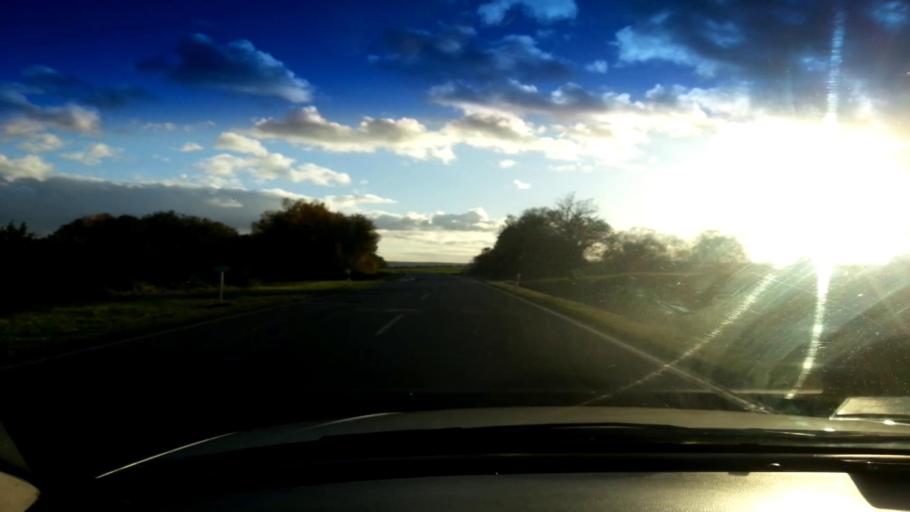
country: DE
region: Bavaria
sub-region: Upper Franconia
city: Zapfendorf
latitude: 50.0366
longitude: 10.9155
